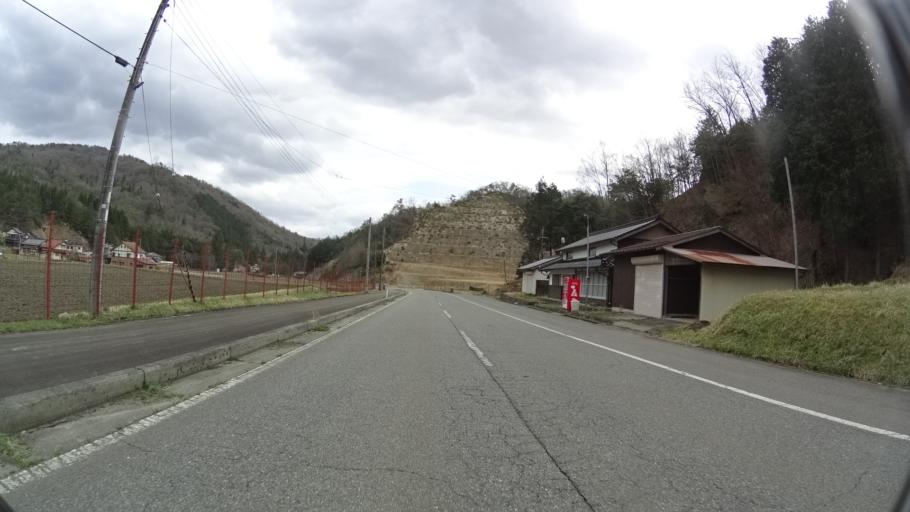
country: JP
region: Hyogo
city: Toyooka
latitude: 35.4845
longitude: 134.9239
